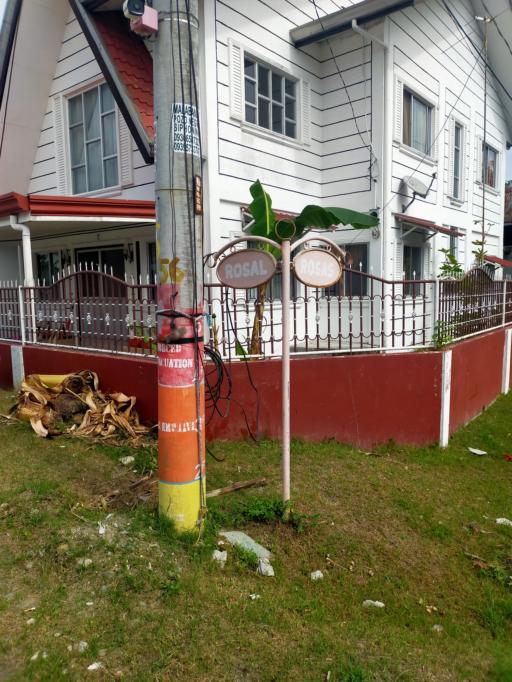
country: PH
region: Central Luzon
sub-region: Province of Pampanga
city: Pau
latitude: 15.0077
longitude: 120.7146
